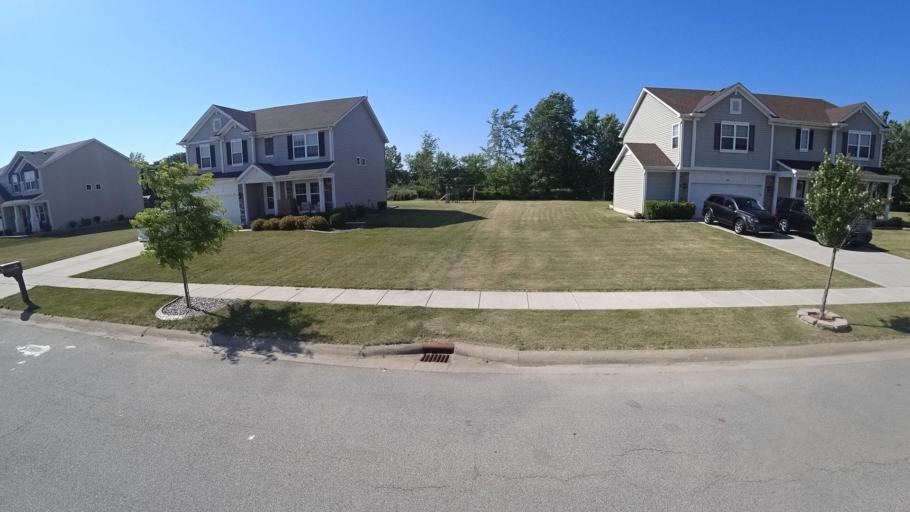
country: US
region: Indiana
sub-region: Porter County
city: Burns Harbor
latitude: 41.6034
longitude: -87.1076
